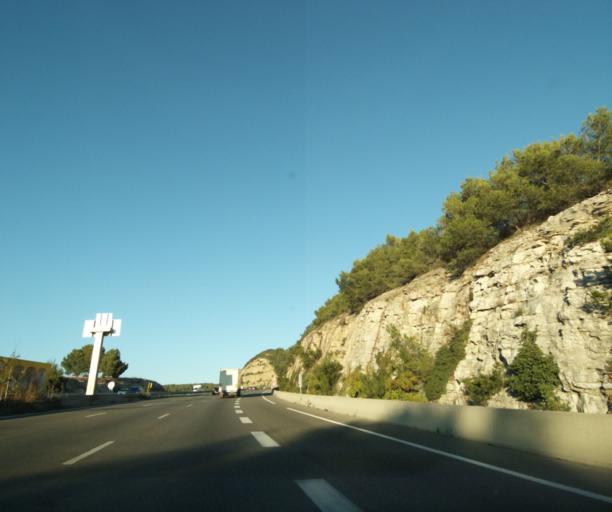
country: FR
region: Provence-Alpes-Cote d'Azur
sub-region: Departement des Bouches-du-Rhone
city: Roquefort-la-Bedoule
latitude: 43.2280
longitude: 5.5834
